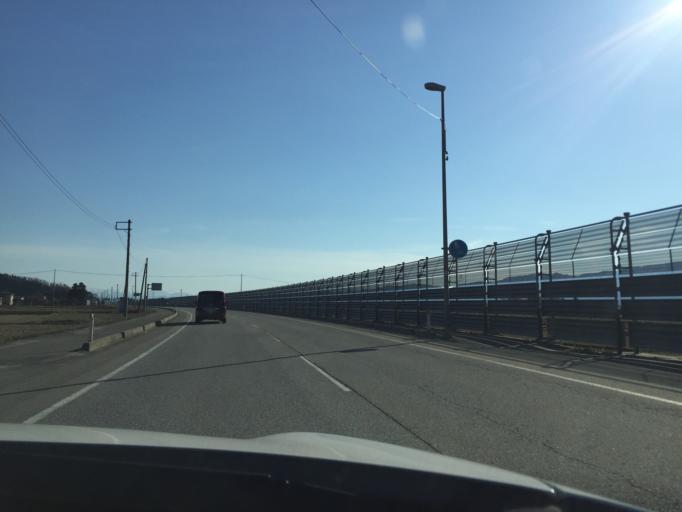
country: JP
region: Yamagata
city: Nagai
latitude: 38.1515
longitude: 140.0648
